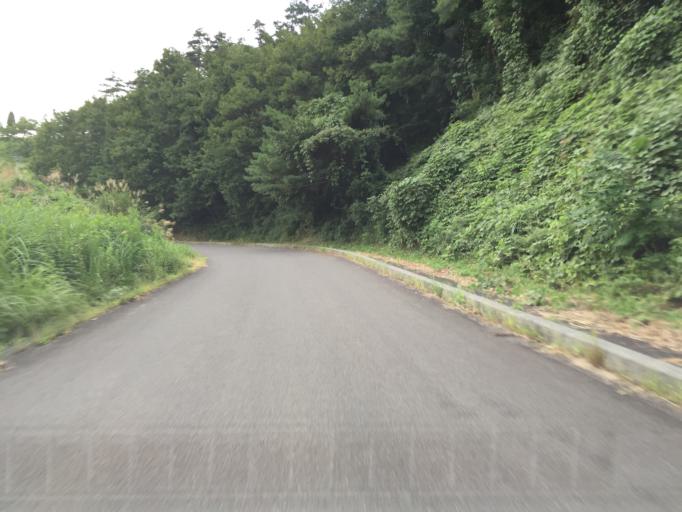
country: JP
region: Fukushima
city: Fukushima-shi
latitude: 37.6687
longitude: 140.5805
